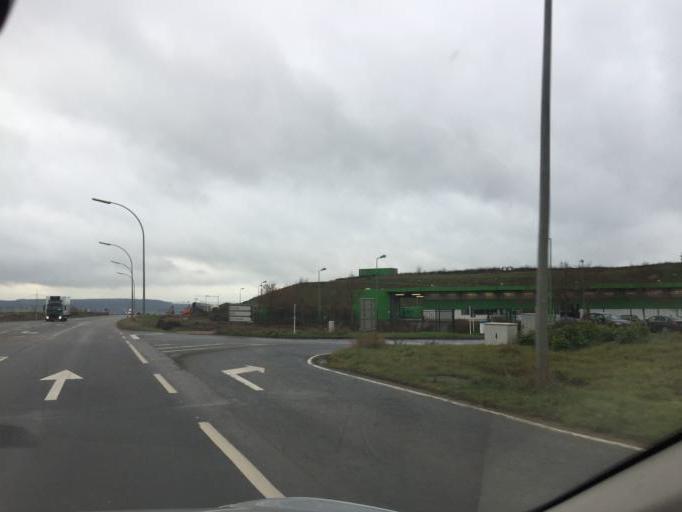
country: LU
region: Diekirch
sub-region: Canton de Diekirch
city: Erpeldange
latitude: 49.8794
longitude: 6.1338
